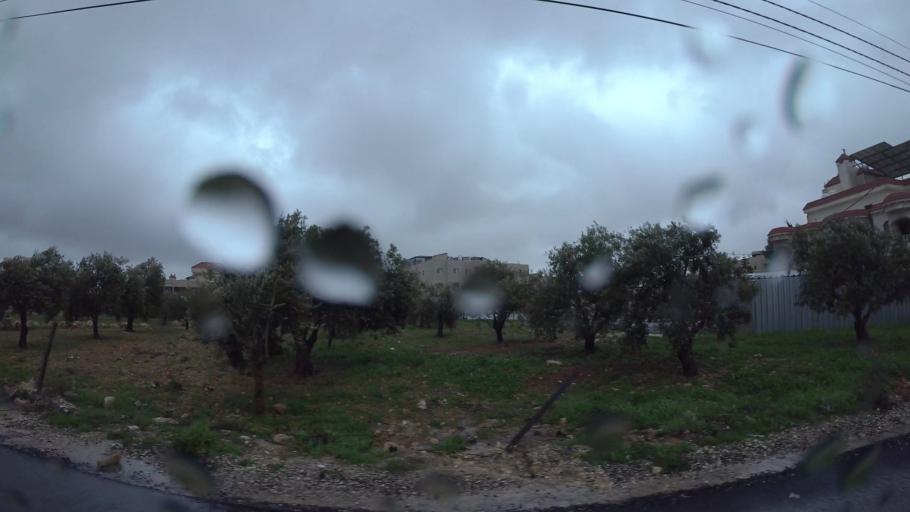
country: JO
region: Amman
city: Al Jubayhah
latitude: 32.0472
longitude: 35.8874
